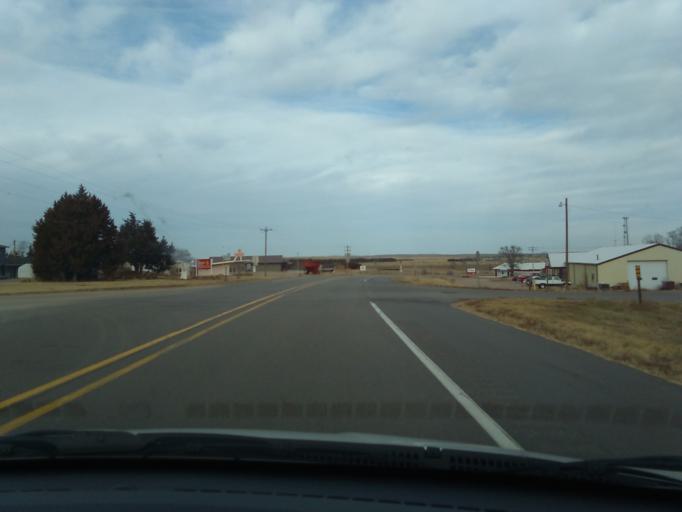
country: US
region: Nebraska
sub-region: Dundy County
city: Benkelman
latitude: 40.0536
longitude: -101.5427
